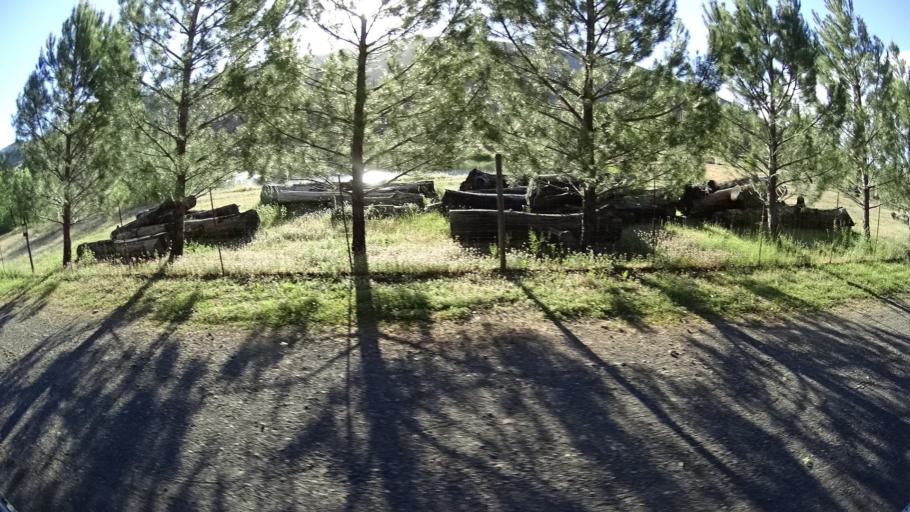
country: US
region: California
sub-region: Lake County
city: Upper Lake
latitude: 39.2341
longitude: -122.9464
